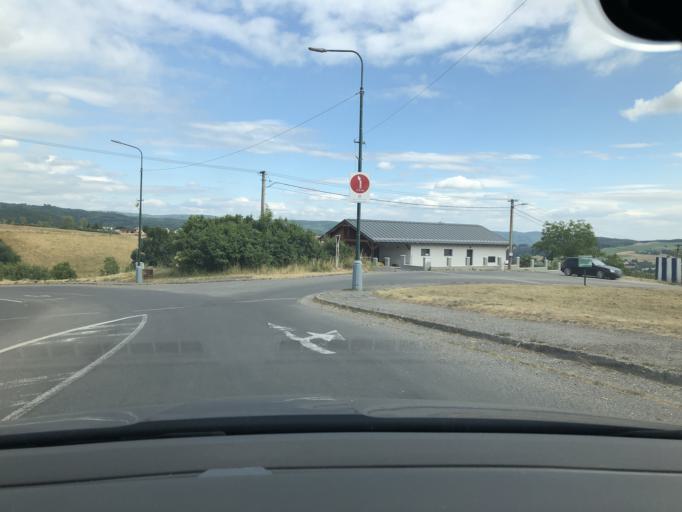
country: SK
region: Banskobystricky
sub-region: Okres Banska Bystrica
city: Banska Stiavnica
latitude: 48.4579
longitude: 18.9066
